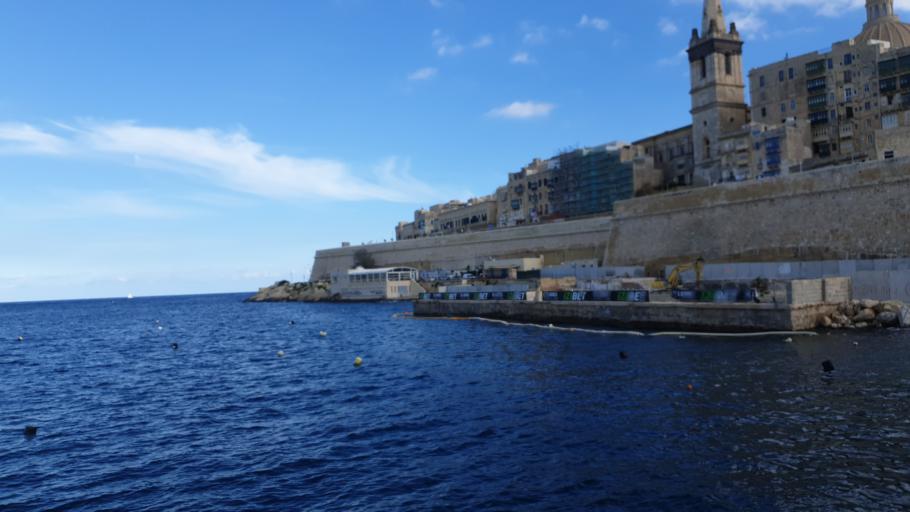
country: MT
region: Il-Furjana
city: Floriana
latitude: 35.9009
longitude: 14.5096
